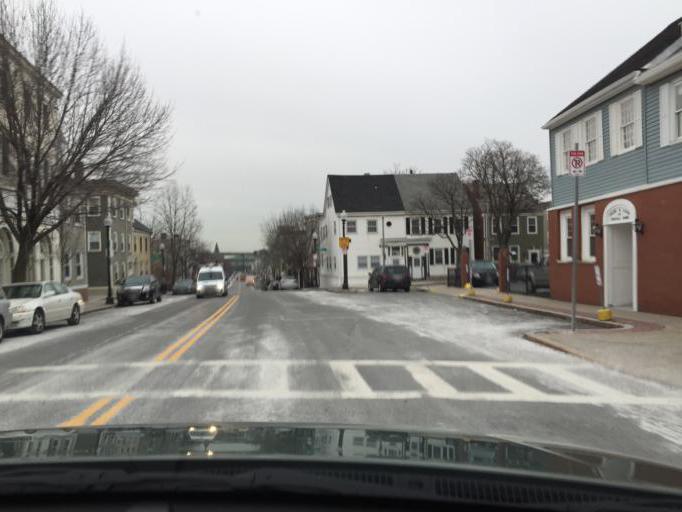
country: US
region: Massachusetts
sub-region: Suffolk County
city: Boston
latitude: 42.3792
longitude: -71.0631
